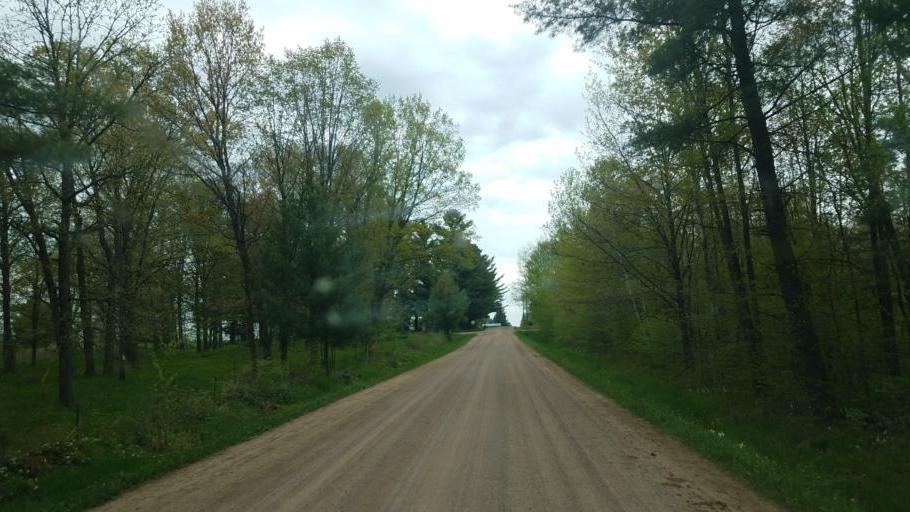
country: US
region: Wisconsin
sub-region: Marathon County
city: Spencer
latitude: 44.6108
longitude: -90.3768
